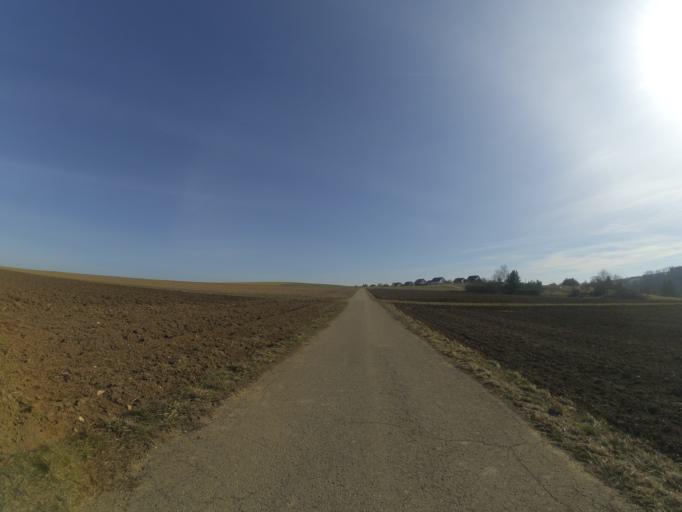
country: DE
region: Baden-Wuerttemberg
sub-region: Tuebingen Region
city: Bernstadt
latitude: 48.4872
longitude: 10.0495
